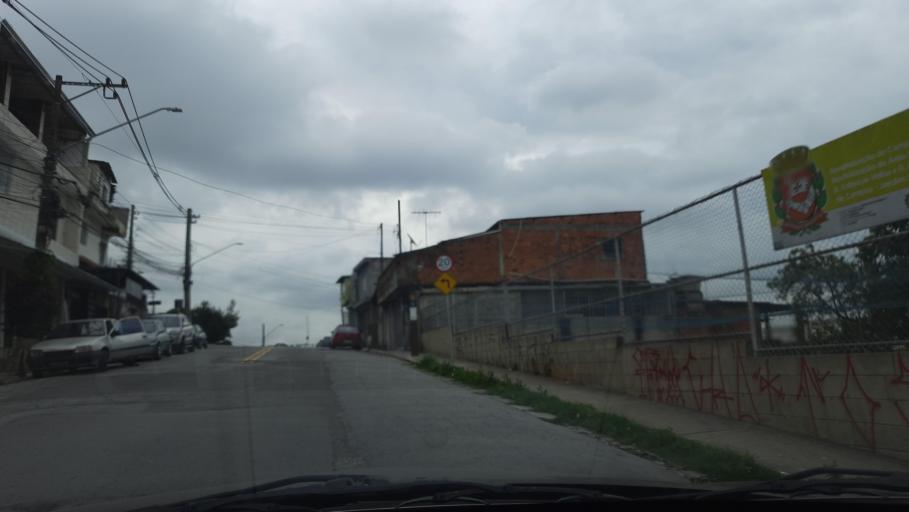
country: BR
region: Sao Paulo
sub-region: Caieiras
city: Caieiras
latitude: -23.4497
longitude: -46.7190
